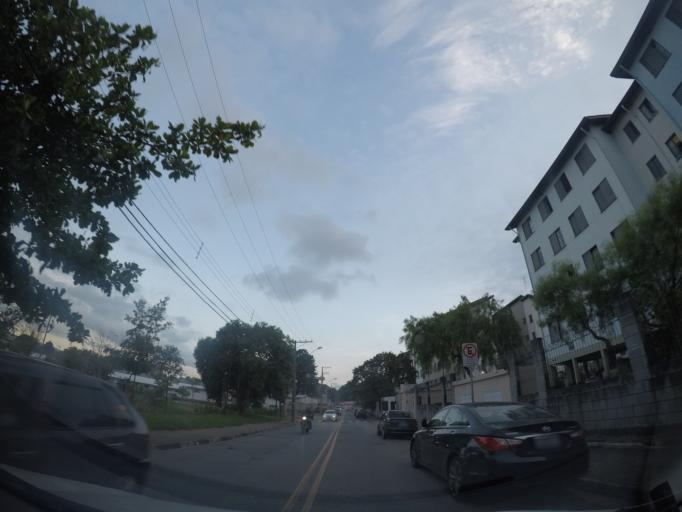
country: BR
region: Sao Paulo
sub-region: Guarulhos
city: Guarulhos
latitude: -23.4560
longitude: -46.4968
